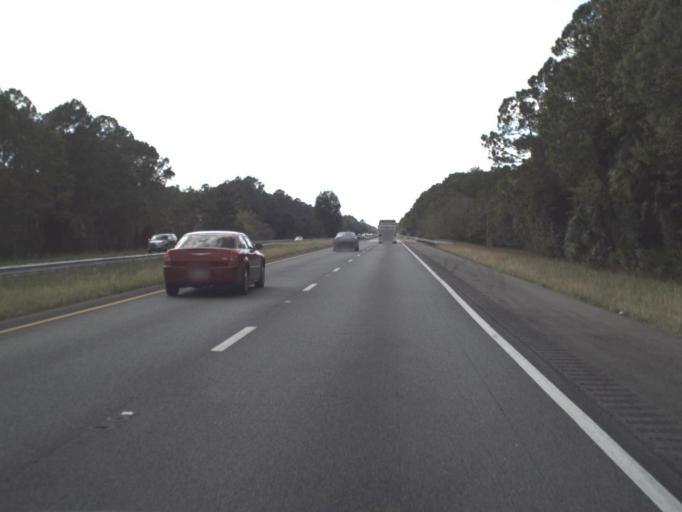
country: US
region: Florida
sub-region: Orange County
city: Christmas
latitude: 28.4528
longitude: -80.9479
